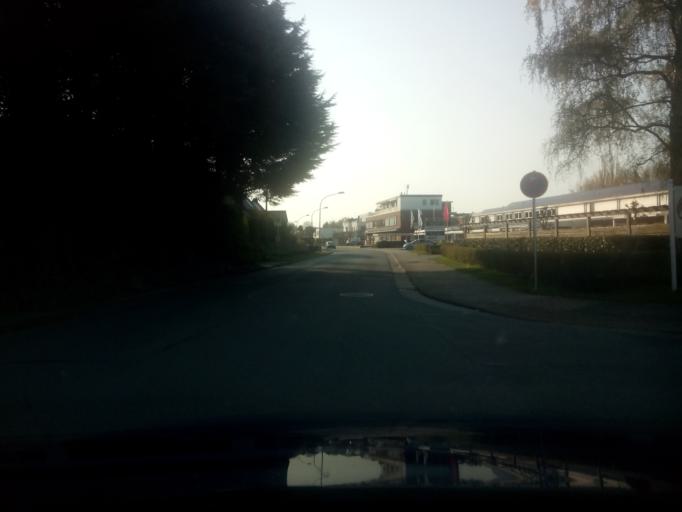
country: DE
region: Lower Saxony
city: Ritterhude
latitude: 53.1857
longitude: 8.7542
